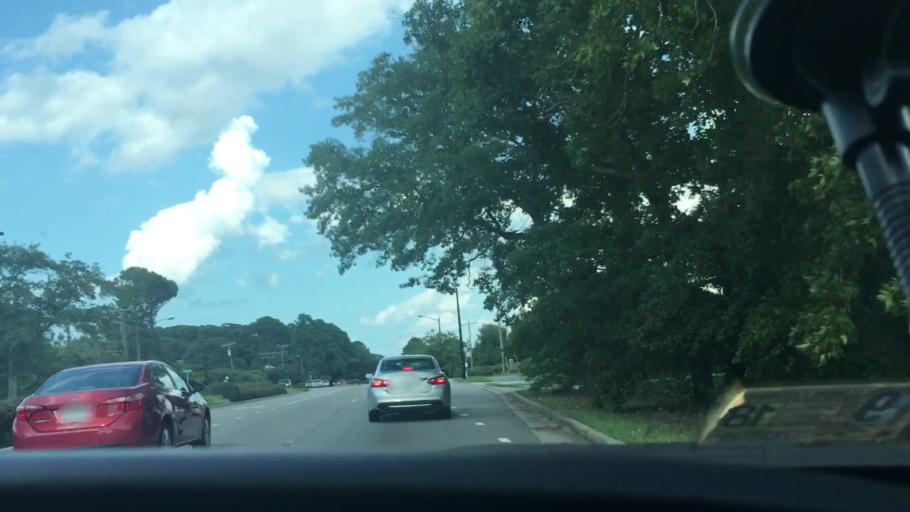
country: US
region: Virginia
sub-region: City of Virginia Beach
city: Virginia Beach
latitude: 36.9053
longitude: -76.1209
